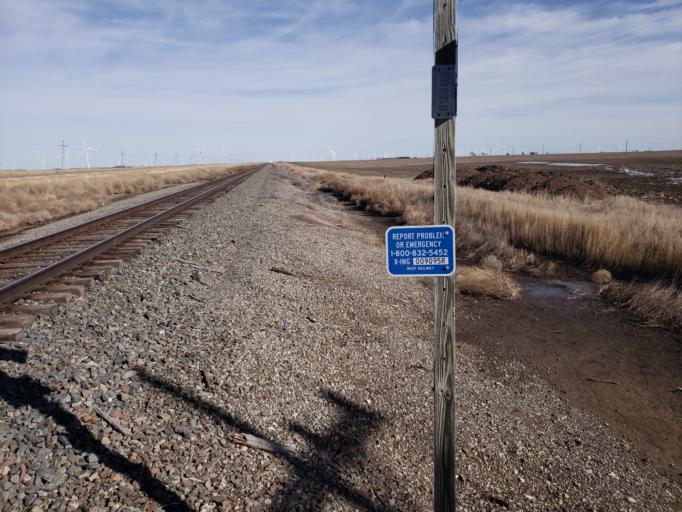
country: US
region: Kansas
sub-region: Ford County
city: Dodge City
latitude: 37.7937
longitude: -99.8693
